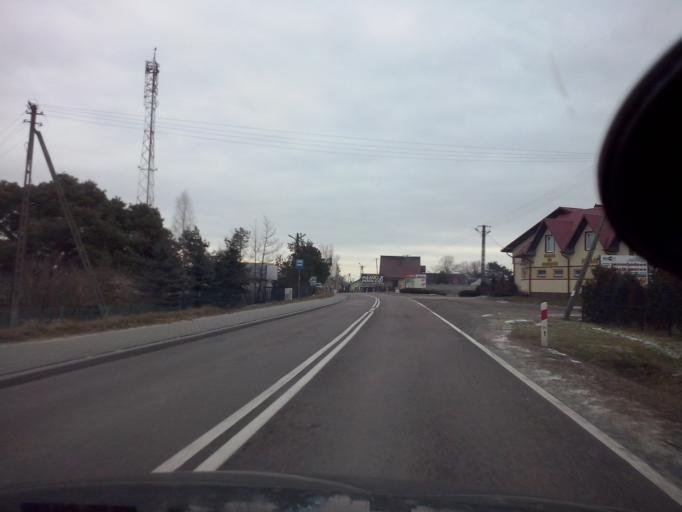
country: PL
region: Lublin Voivodeship
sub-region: Powiat bilgorajski
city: Biszcza
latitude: 50.4943
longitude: 22.6287
